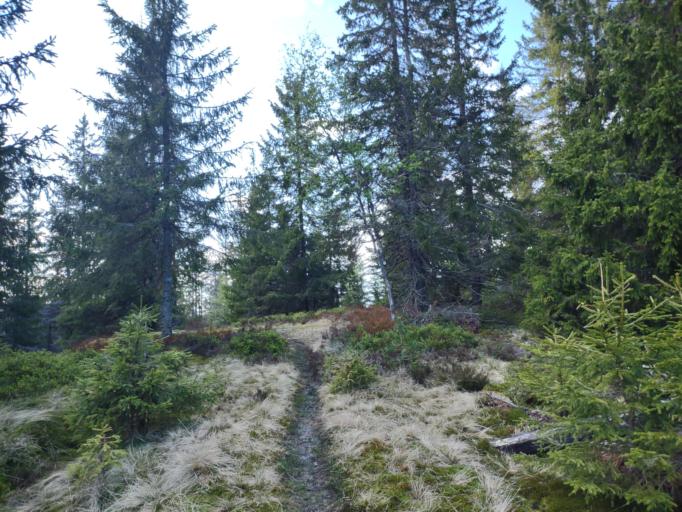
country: NO
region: Akershus
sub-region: Nittedal
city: Aneby
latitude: 60.2537
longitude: 10.8433
